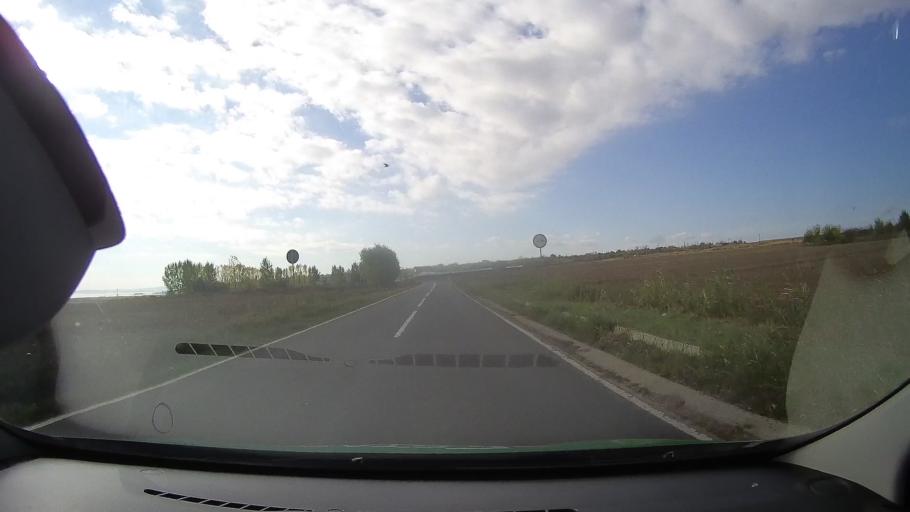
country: RO
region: Tulcea
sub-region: Comuna Sarichioi
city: Sarichioi
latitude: 44.9602
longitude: 28.8591
